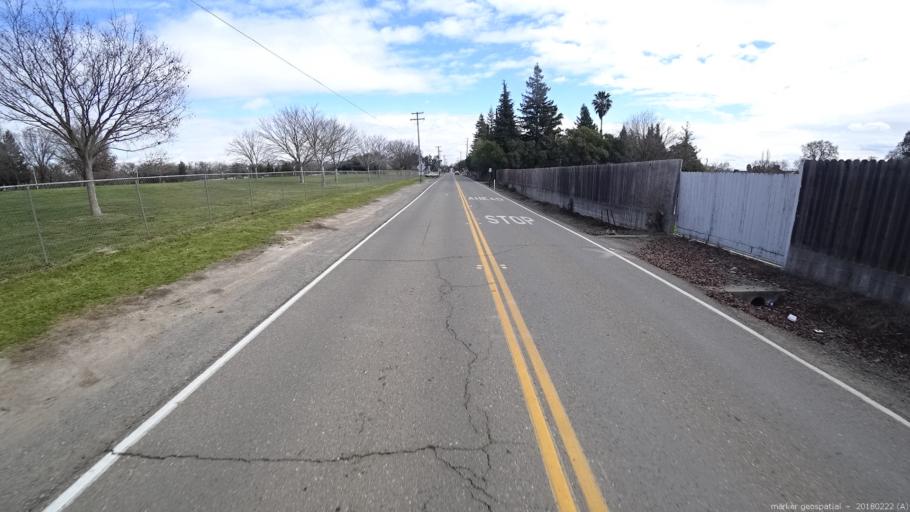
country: US
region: California
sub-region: Sacramento County
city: North Highlands
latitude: 38.7045
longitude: -121.4034
